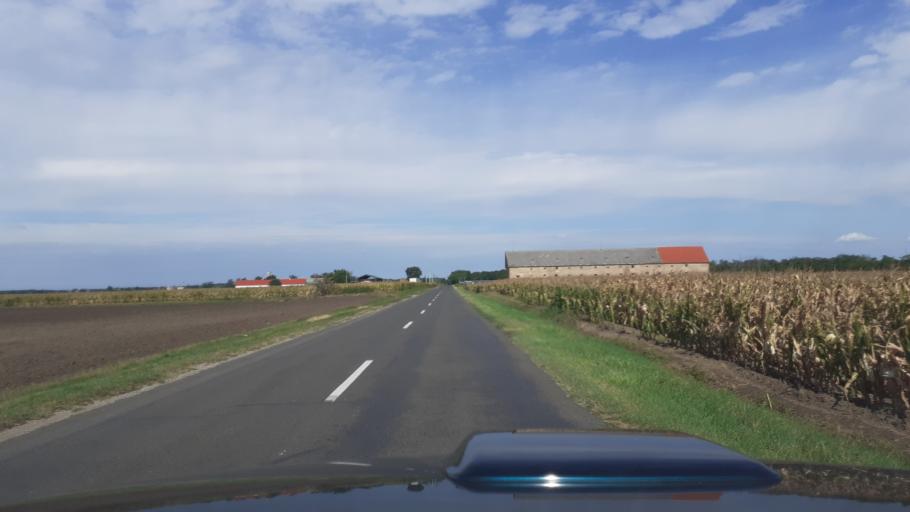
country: HU
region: Fejer
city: Pusztaszabolcs
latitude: 47.1163
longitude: 18.6973
